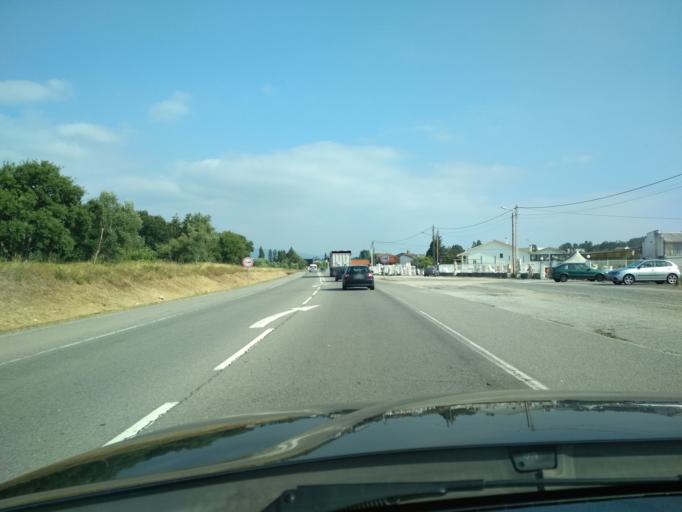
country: PT
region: Aveiro
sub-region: Mealhada
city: Mealhada
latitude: 40.3604
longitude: -8.4525
